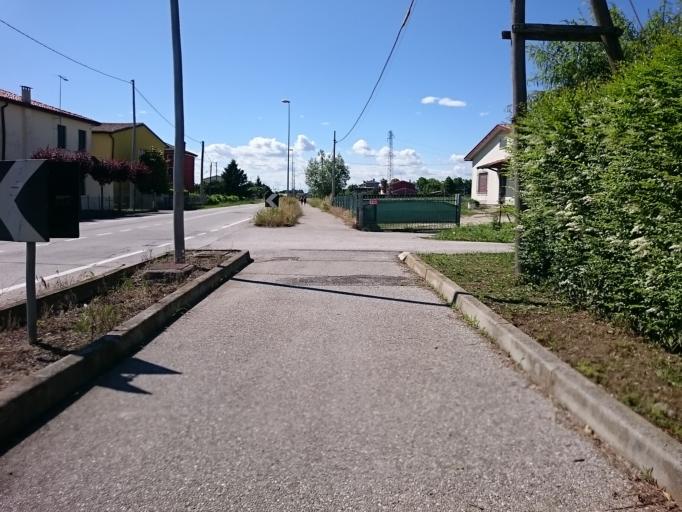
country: IT
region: Veneto
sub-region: Provincia di Venezia
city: Campolongo Maggiore
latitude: 45.3199
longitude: 12.0341
